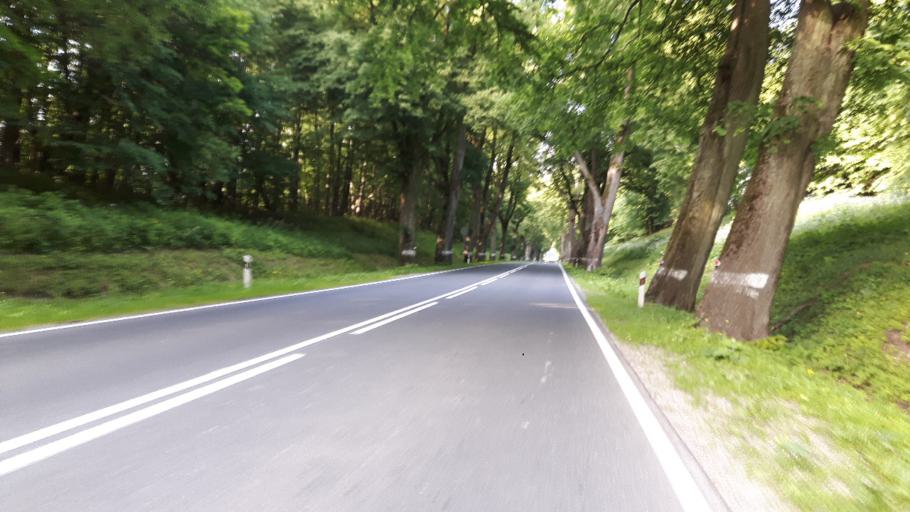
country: RU
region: Kaliningrad
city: Ladushkin
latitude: 54.5269
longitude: 20.1211
